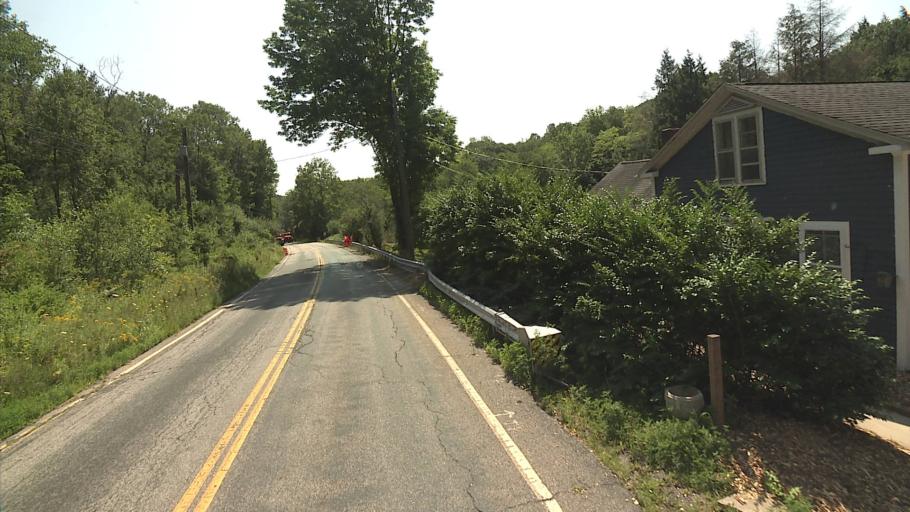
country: US
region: Connecticut
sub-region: Litchfield County
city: Winchester Center
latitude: 41.9169
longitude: -73.1938
